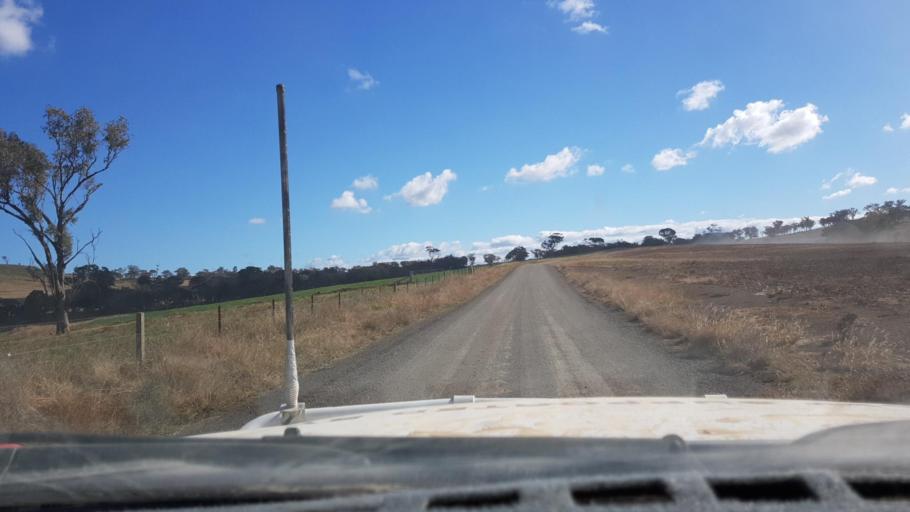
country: AU
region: New South Wales
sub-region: Narrabri
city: Blair Athol
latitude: -30.5601
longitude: 150.4633
